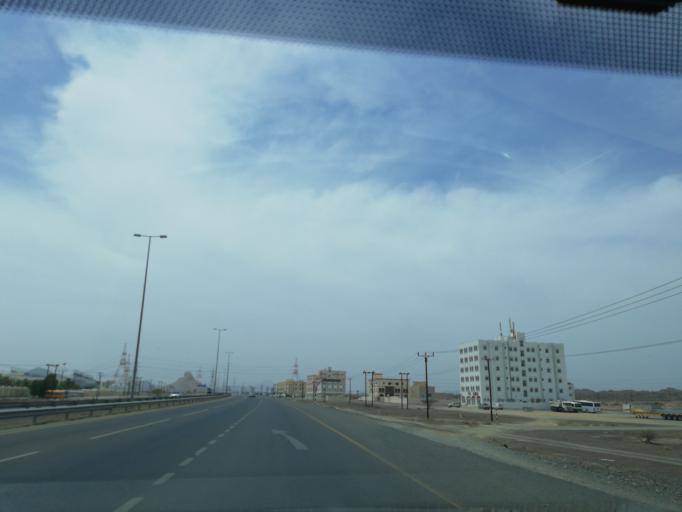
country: OM
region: Muhafazat ad Dakhiliyah
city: Nizwa
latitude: 22.8593
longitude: 57.5163
